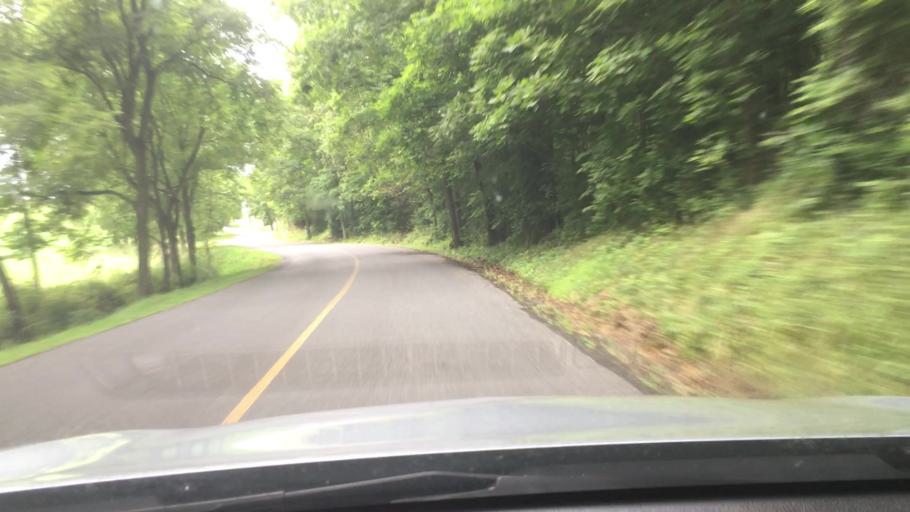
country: US
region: Pennsylvania
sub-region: Franklin County
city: Greencastle
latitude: 39.8629
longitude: -77.7994
